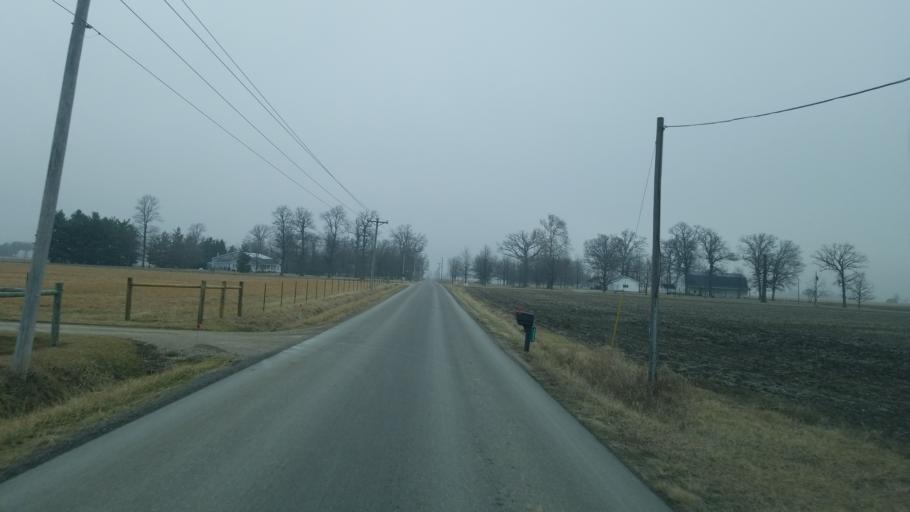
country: US
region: Indiana
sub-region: Adams County
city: Berne
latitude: 40.6836
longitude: -84.9944
